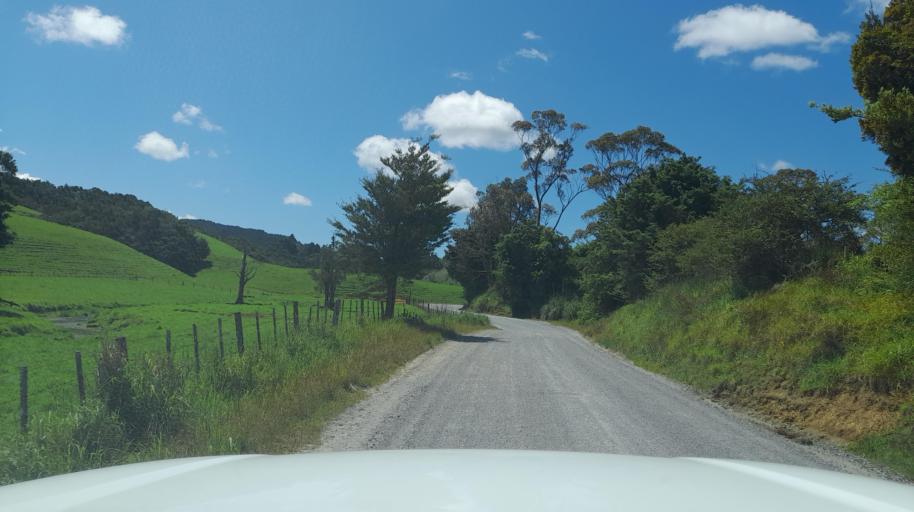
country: NZ
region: Northland
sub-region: Far North District
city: Kaitaia
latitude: -35.1146
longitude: 173.3947
